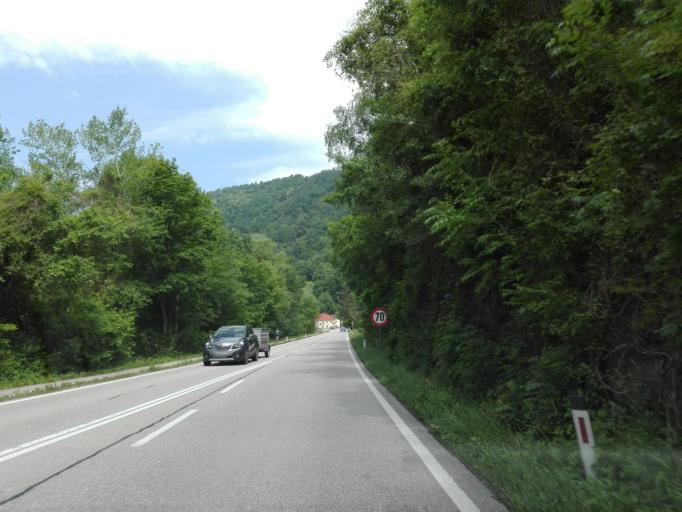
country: AT
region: Upper Austria
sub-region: Politischer Bezirk Rohrbach
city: Kleinzell im Muehlkreis
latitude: 48.3741
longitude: 13.9586
